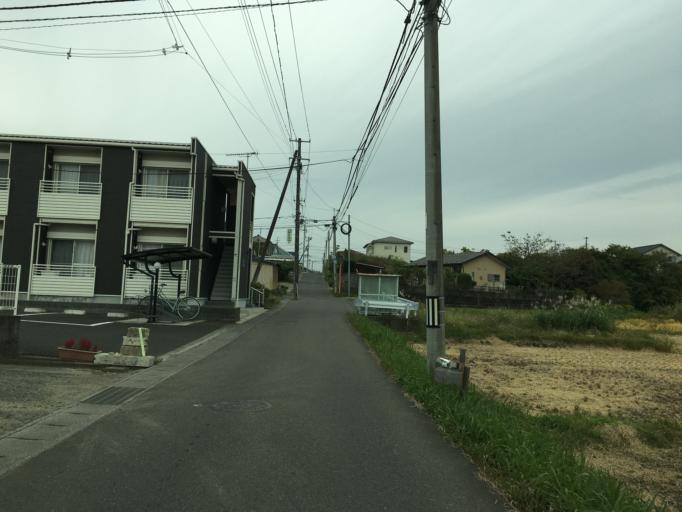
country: JP
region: Fukushima
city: Hobaramachi
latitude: 37.8239
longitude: 140.5055
